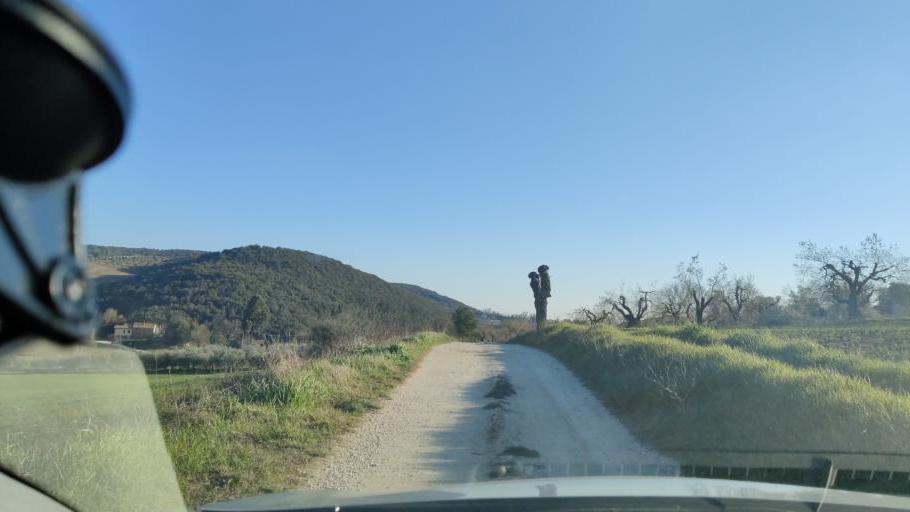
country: IT
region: Umbria
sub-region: Provincia di Terni
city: Fornole
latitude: 42.5603
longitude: 12.4494
